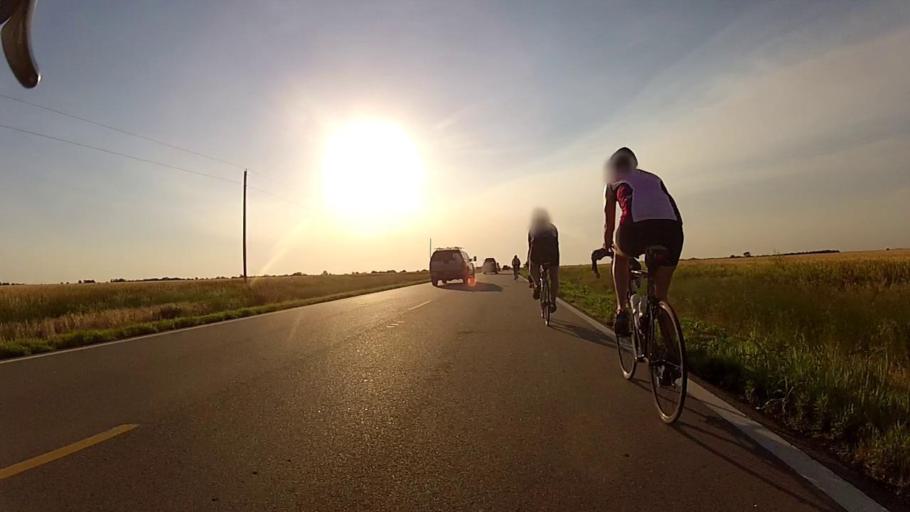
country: US
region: Kansas
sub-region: Harper County
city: Anthony
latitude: 37.1542
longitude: -97.8334
